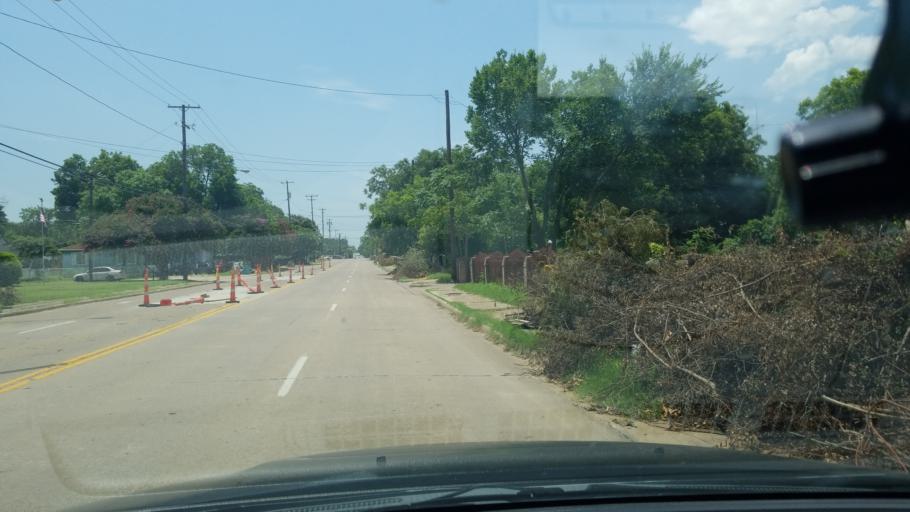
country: US
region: Texas
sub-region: Dallas County
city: Balch Springs
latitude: 32.7381
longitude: -96.6787
